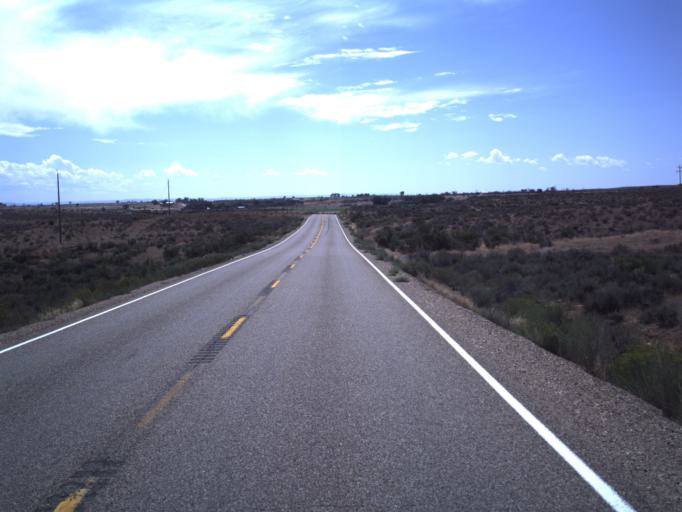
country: US
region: Utah
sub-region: Uintah County
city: Maeser
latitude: 40.2702
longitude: -109.6831
